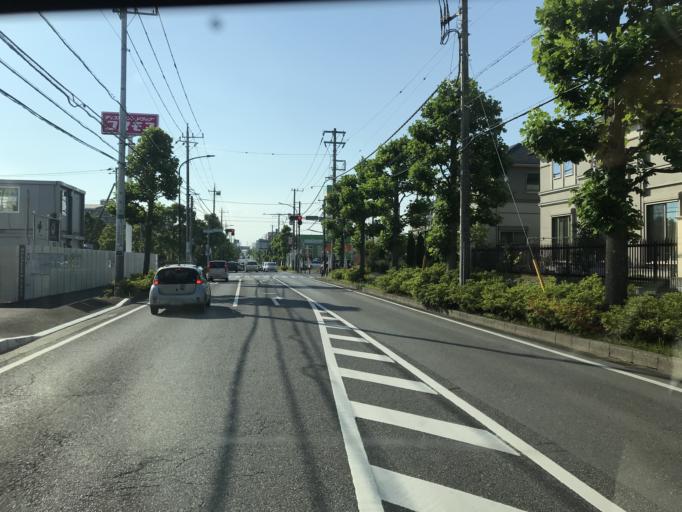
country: JP
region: Chiba
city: Chiba
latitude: 35.5451
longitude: 140.1816
